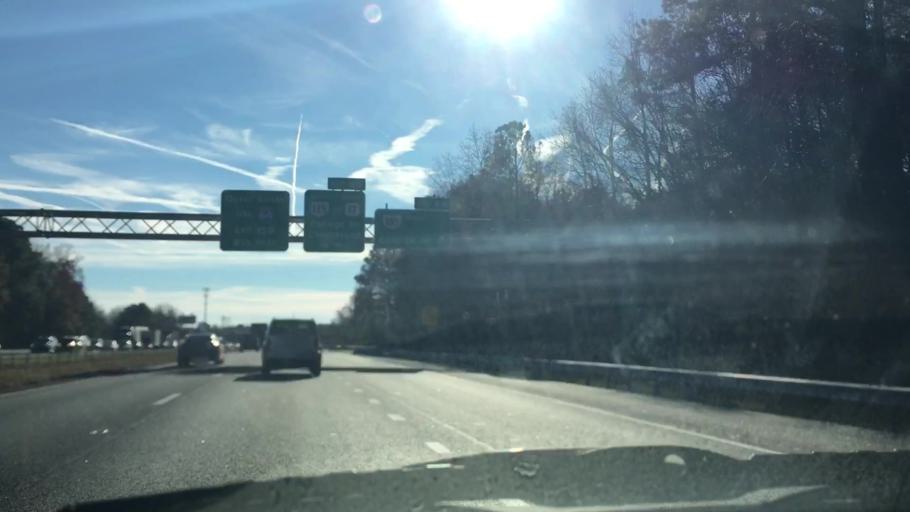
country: US
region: Virginia
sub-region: City of Newport News
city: Newport News
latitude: 36.8918
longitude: -76.4276
